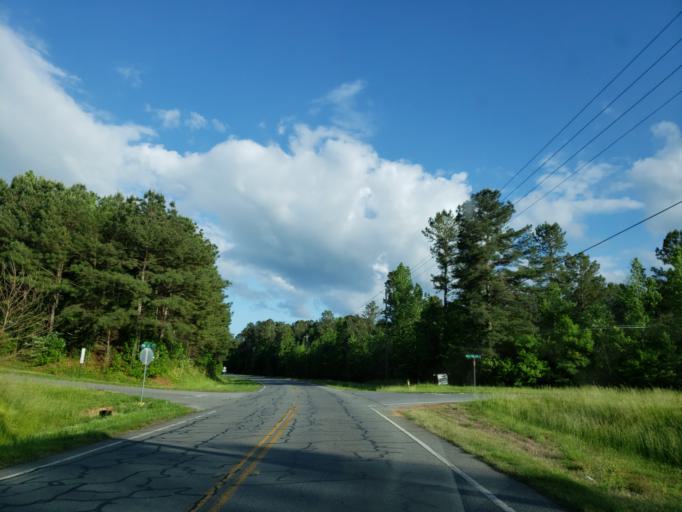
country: US
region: Georgia
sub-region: Bartow County
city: Rydal
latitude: 34.3403
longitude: -84.7428
